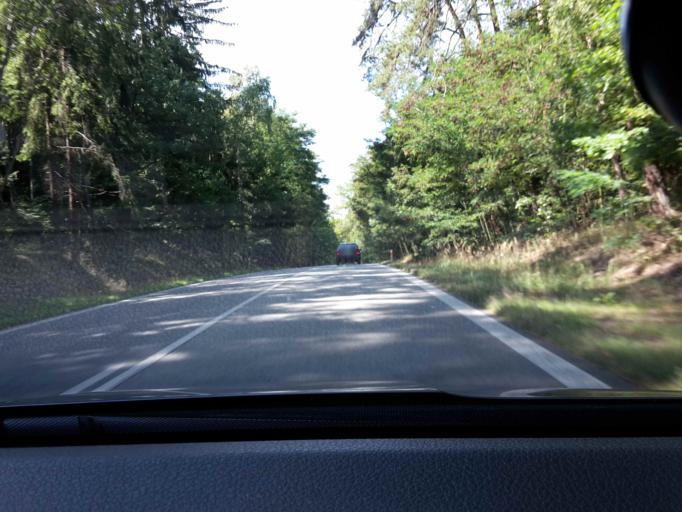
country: CZ
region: Jihocesky
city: Kardasova Recice
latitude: 49.1748
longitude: 14.8872
